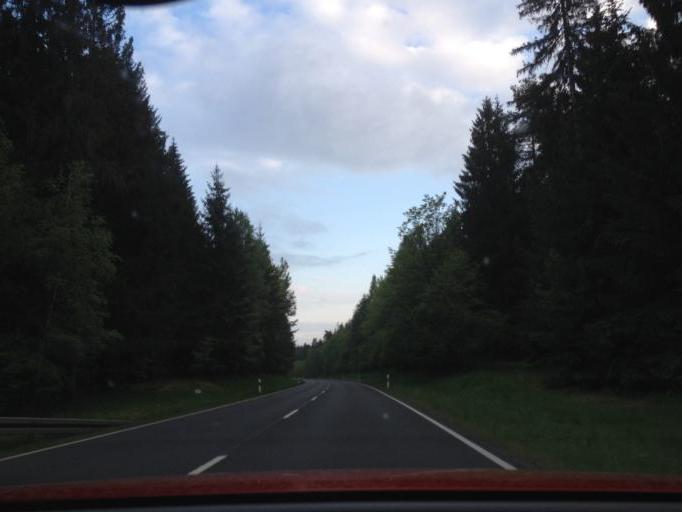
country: DE
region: Bavaria
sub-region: Upper Palatinate
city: Kohlberg
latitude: 49.5868
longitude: 11.9936
